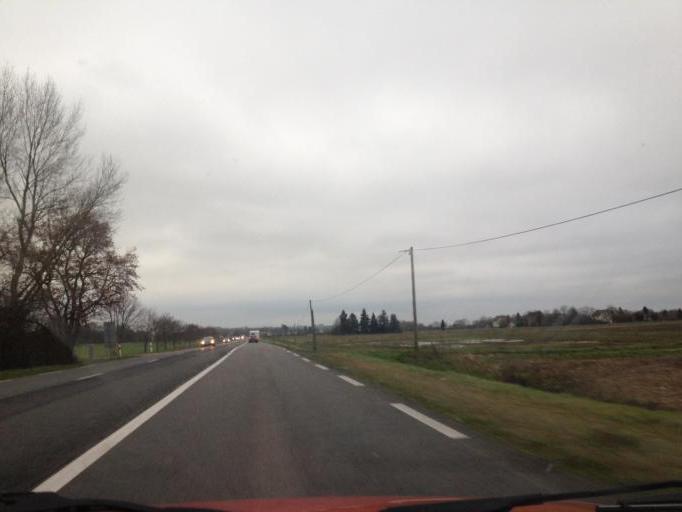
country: FR
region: Auvergne
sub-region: Departement de l'Allier
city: Varennes-sur-Allier
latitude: 46.3648
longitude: 3.3676
